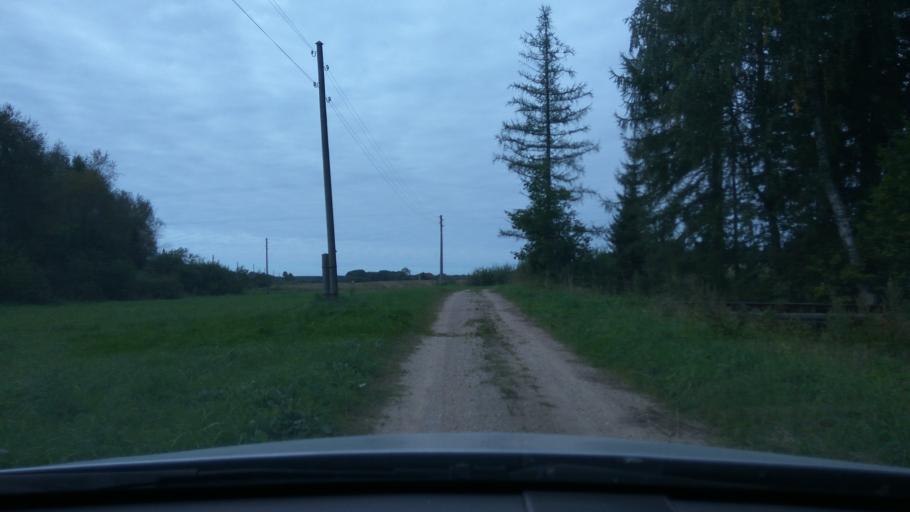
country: LV
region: Kuldigas Rajons
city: Kuldiga
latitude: 57.2414
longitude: 21.9619
